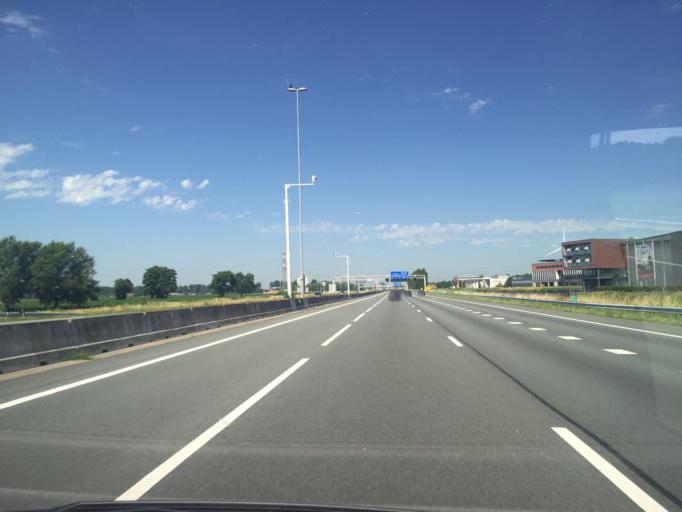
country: NL
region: Gelderland
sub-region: Gemeente Ede
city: Ede
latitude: 52.0197
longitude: 5.6283
